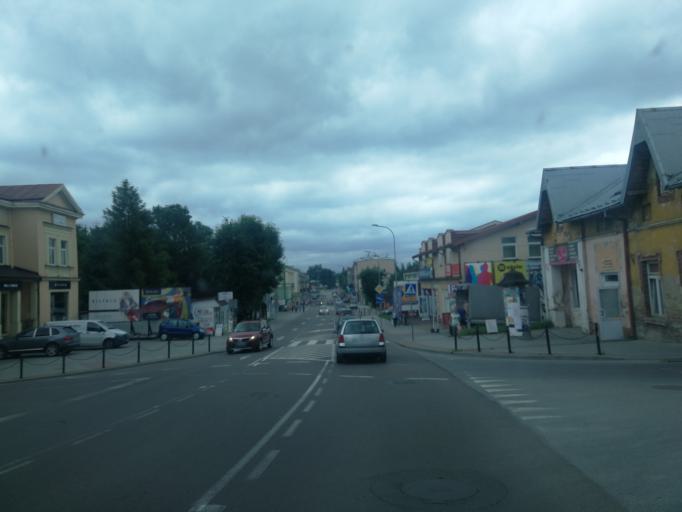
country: PL
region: Subcarpathian Voivodeship
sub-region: Powiat sanocki
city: Sanok
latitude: 49.5566
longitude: 22.2035
